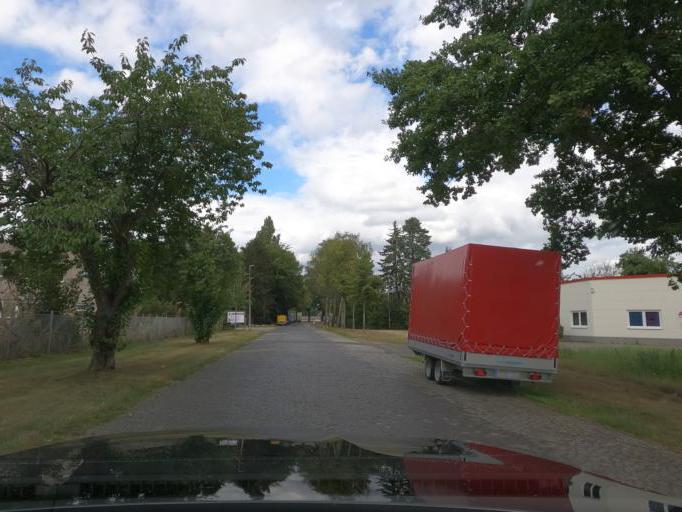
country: DE
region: Lower Saxony
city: Isernhagen Farster Bauerschaft
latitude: 52.4401
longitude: 9.8820
